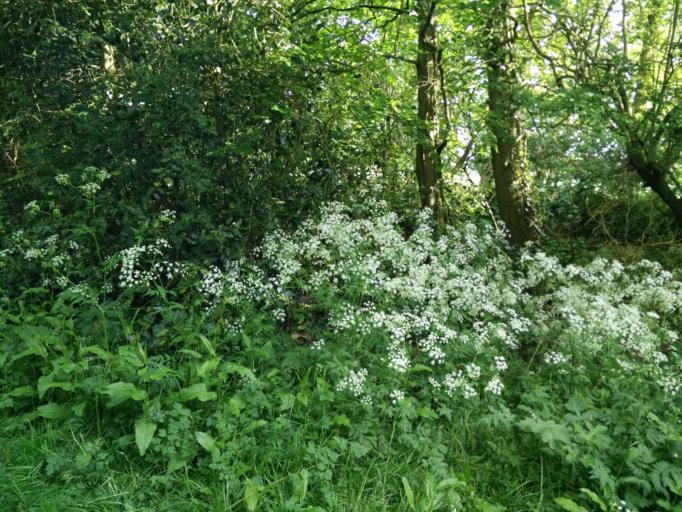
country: GB
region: England
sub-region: North Yorkshire
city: Strensall
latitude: 54.0871
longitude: -1.0036
